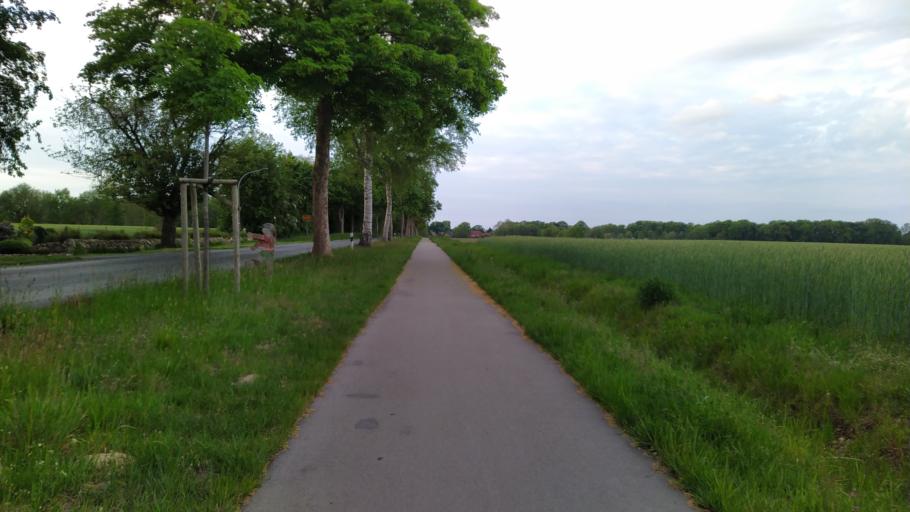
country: DE
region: Lower Saxony
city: Ahlerstedt
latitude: 53.3961
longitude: 9.4040
